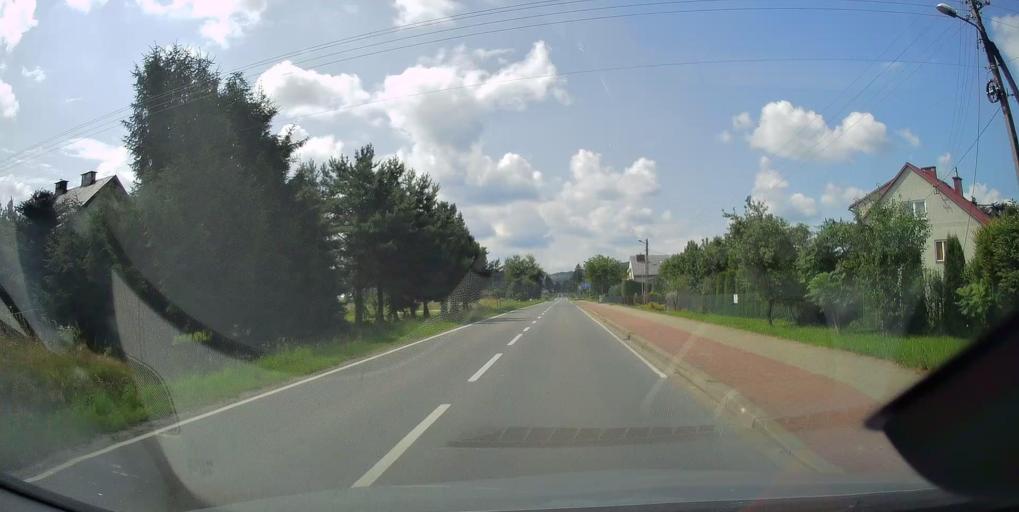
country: PL
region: Lesser Poland Voivodeship
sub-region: Powiat tarnowski
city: Zakliczyn
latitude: 49.8549
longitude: 20.8130
